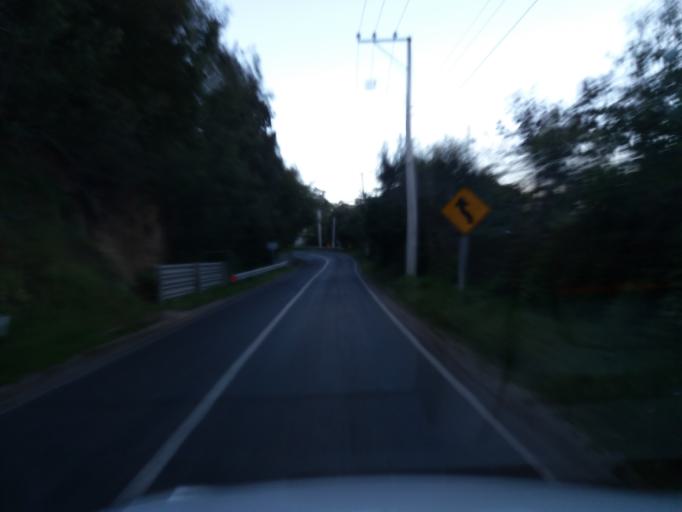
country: CL
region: Valparaiso
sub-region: Provincia de Quillota
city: Quillota
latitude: -32.8787
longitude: -71.2744
